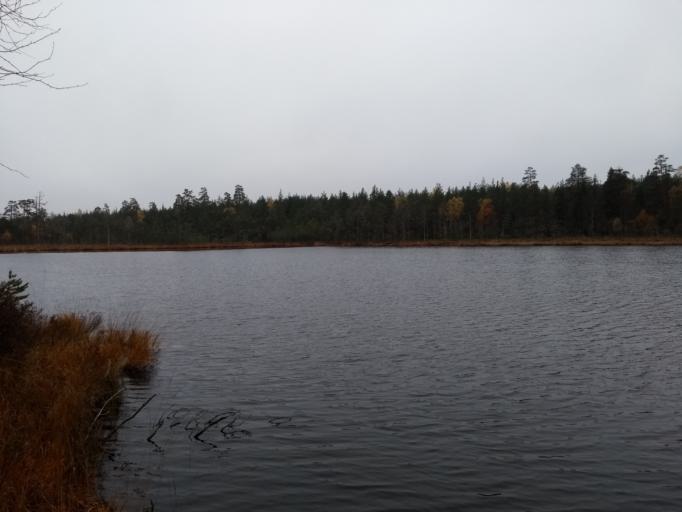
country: SE
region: Soedermanland
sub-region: Nykopings Kommun
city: Stigtomta
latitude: 58.6722
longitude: 16.6970
